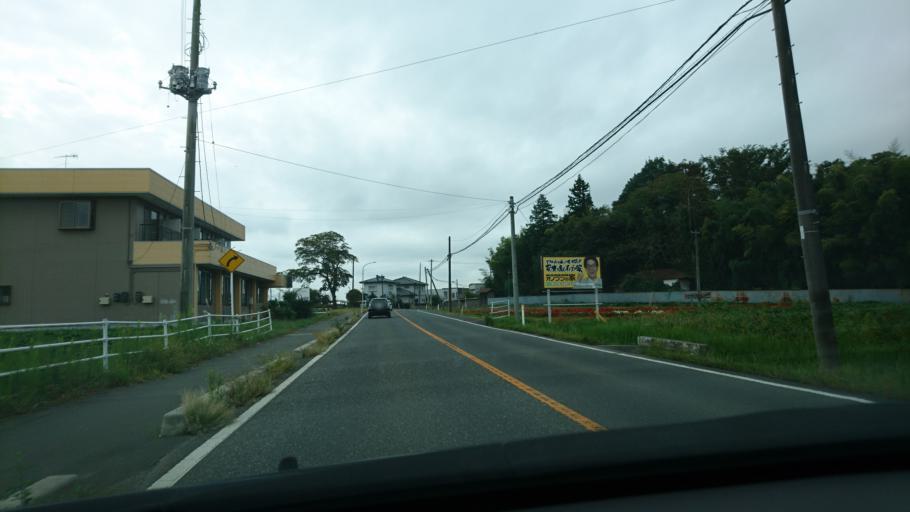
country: JP
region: Iwate
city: Ichinoseki
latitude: 38.7609
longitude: 141.0779
